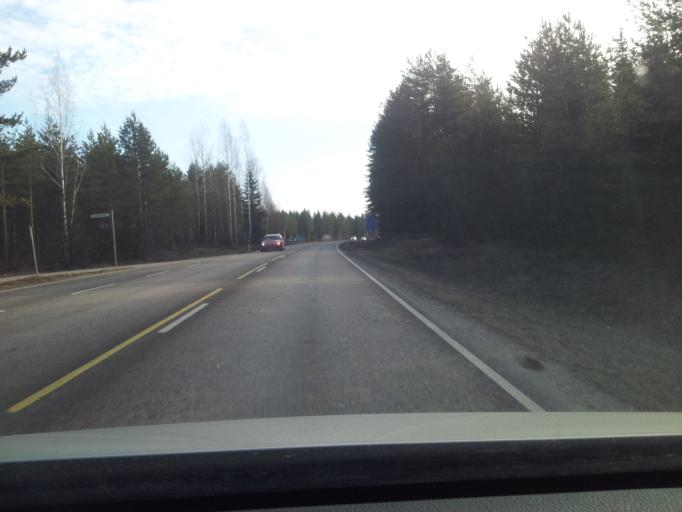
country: FI
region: Kymenlaakso
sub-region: Kouvola
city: Kouvola
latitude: 60.8553
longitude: 26.5520
